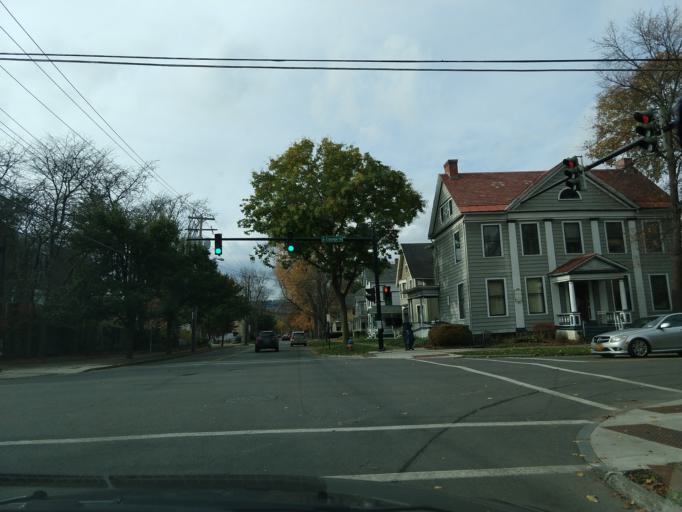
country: US
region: New York
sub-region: Tompkins County
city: Ithaca
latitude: 42.4426
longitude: -76.4989
